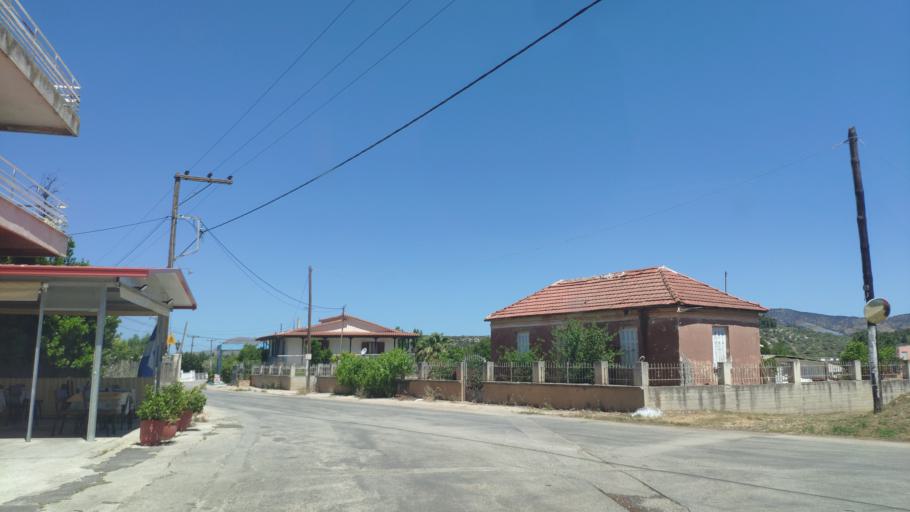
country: GR
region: Peloponnese
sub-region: Nomos Korinthias
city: Athikia
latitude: 37.8205
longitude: 22.9234
